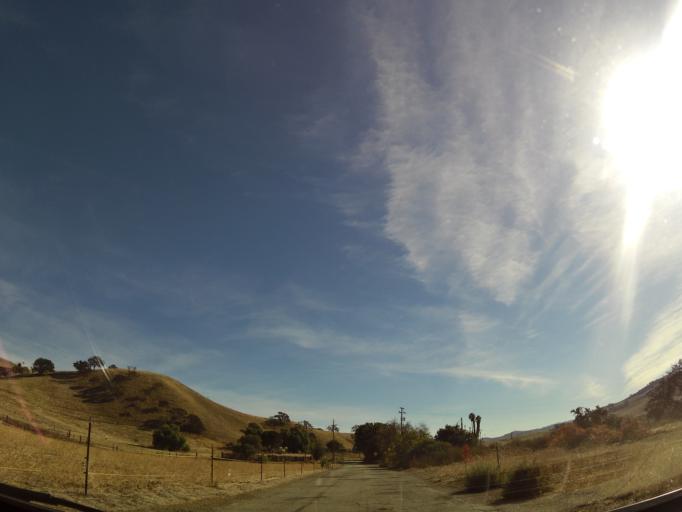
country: US
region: California
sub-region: San Benito County
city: Ridgemark
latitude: 36.7813
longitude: -121.3542
